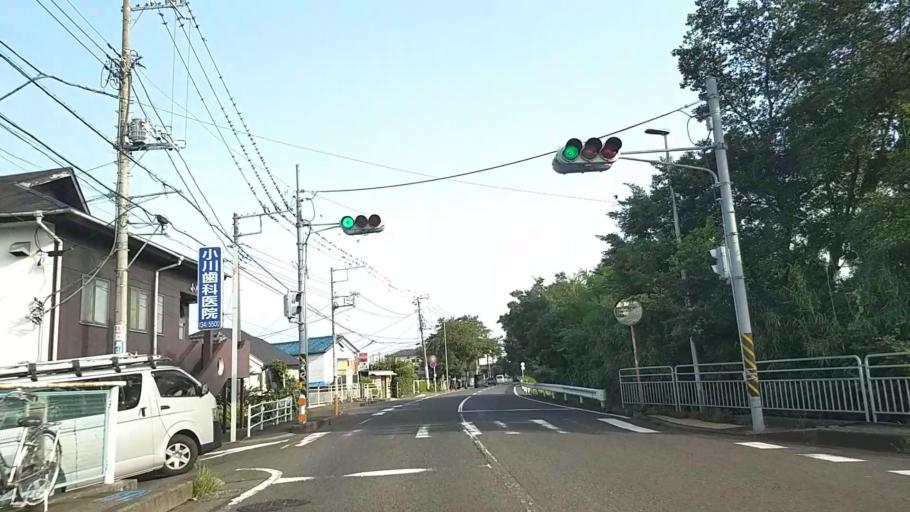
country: JP
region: Kanagawa
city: Hiratsuka
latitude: 35.3434
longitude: 139.3209
